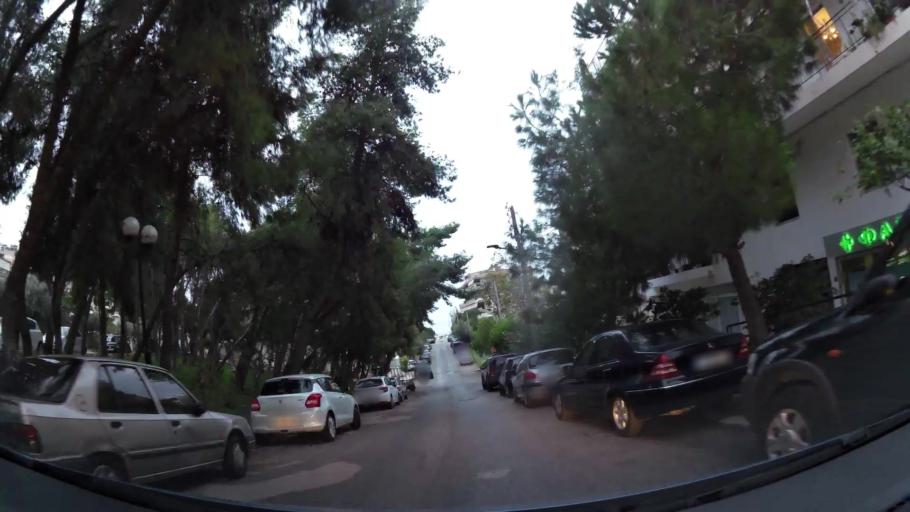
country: GR
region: Attica
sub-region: Nomarchia Athinas
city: Agios Dimitrios
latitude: 37.9381
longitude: 23.7449
